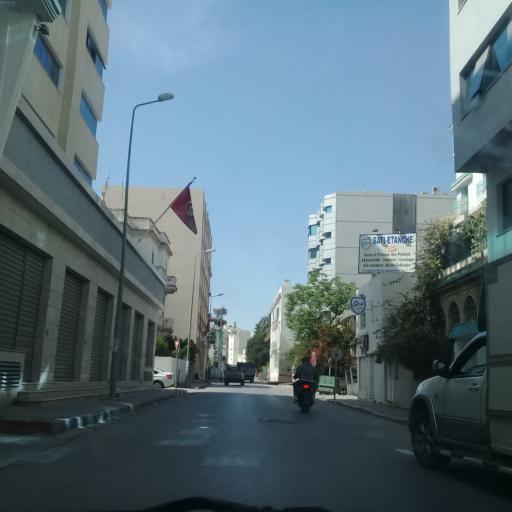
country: TN
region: Tunis
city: Tunis
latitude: 36.8167
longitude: 10.1798
